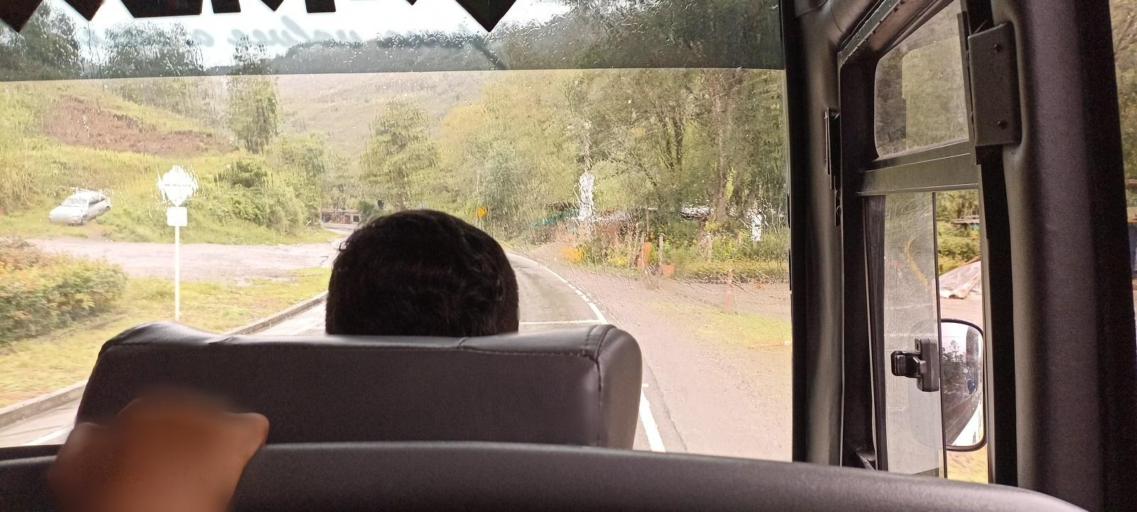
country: CO
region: Boyaca
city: Somondoco
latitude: 5.0068
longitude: -73.4025
